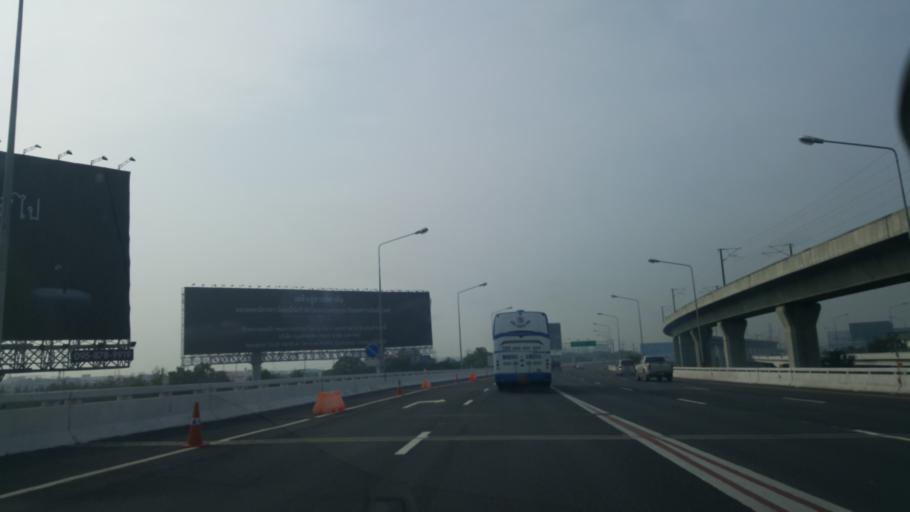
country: TH
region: Bangkok
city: Lat Krabang
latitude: 13.7261
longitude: 100.7605
